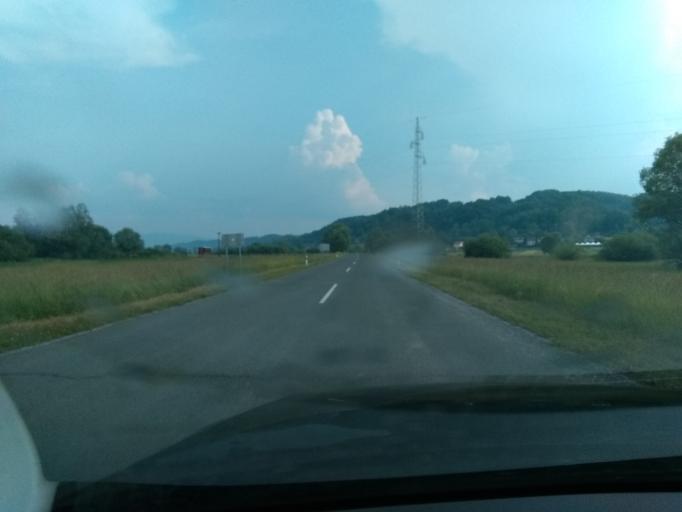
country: HR
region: Krapinsko-Zagorska
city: Pregrada
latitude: 46.0674
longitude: 15.7936
